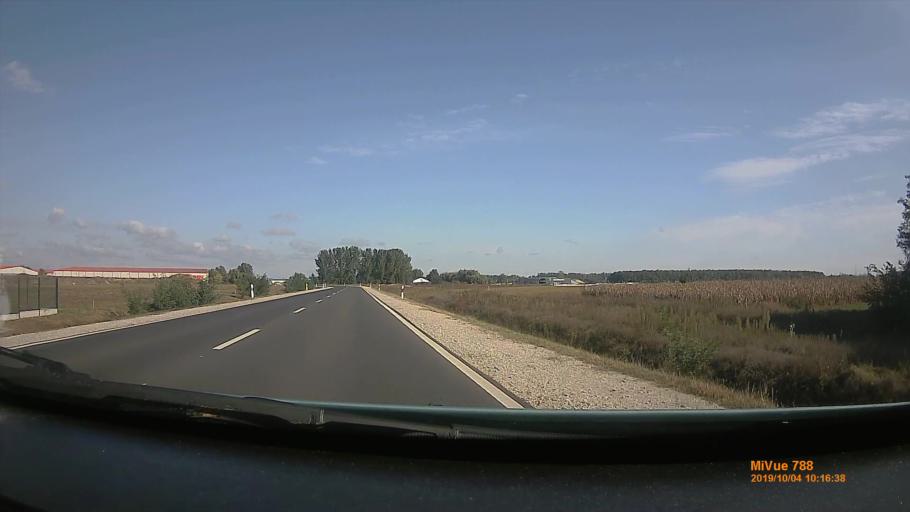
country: HU
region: Szabolcs-Szatmar-Bereg
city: Nyiregyhaza
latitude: 47.9510
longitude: 21.6544
